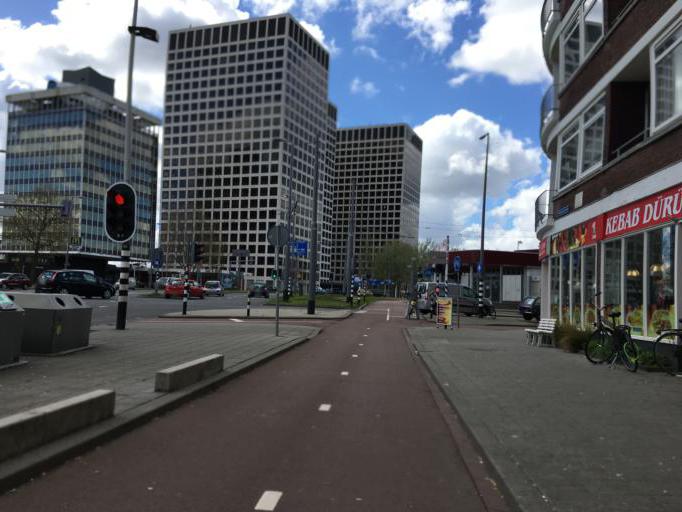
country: NL
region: South Holland
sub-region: Gemeente Rotterdam
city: Delfshaven
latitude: 51.9134
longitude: 4.4339
